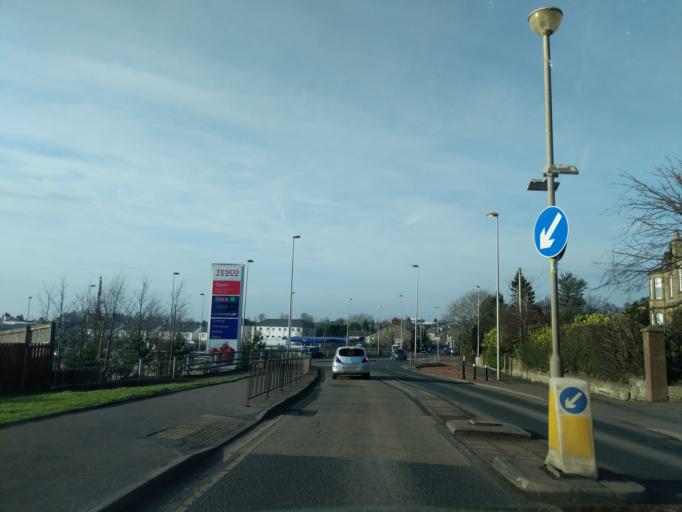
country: GB
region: Scotland
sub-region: South Lanarkshire
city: Carluke
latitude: 55.7284
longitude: -3.8349
